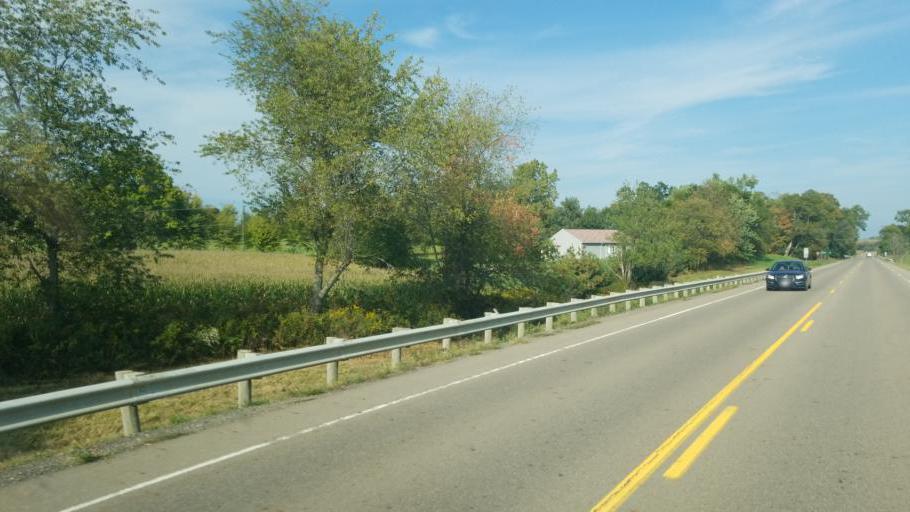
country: US
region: Ohio
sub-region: Licking County
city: Utica
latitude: 40.2669
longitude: -82.3931
